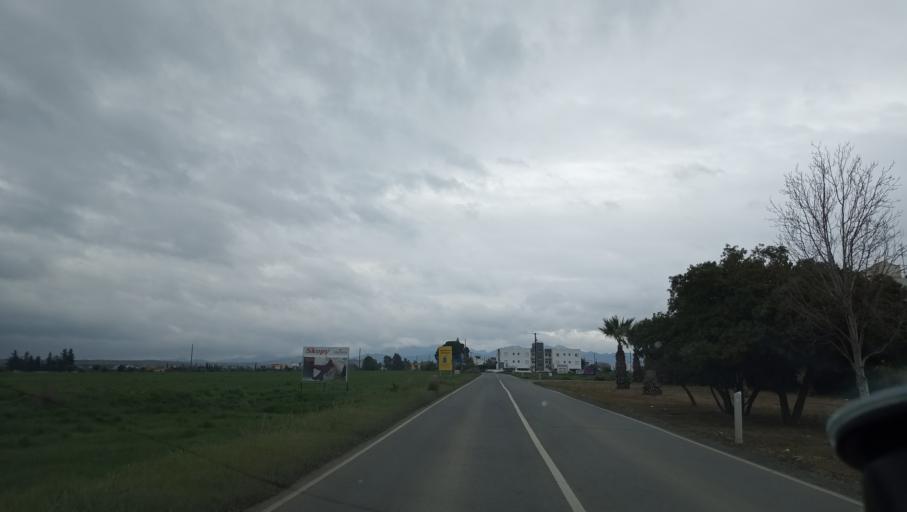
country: CY
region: Lefkosia
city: Pano Deftera
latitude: 35.0778
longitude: 33.2713
